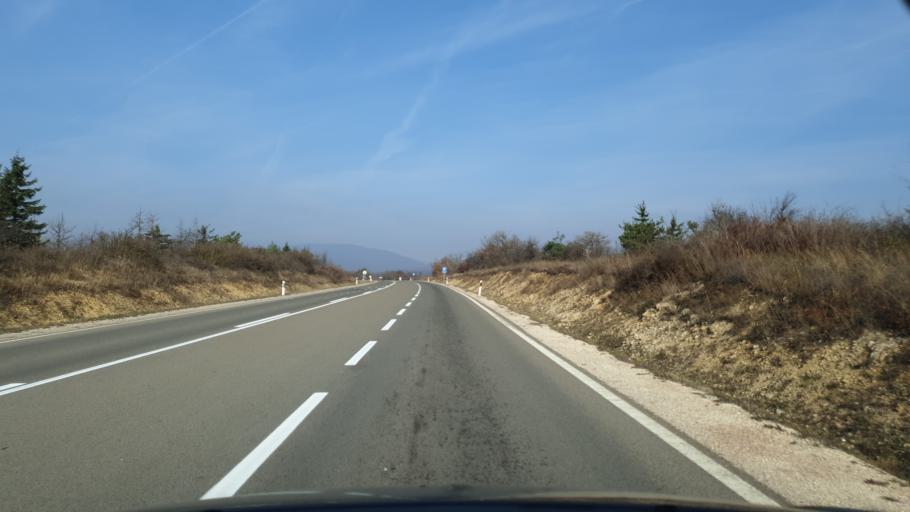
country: RS
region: Central Serbia
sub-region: Zajecarski Okrug
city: Boljevac
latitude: 43.8210
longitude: 21.7258
